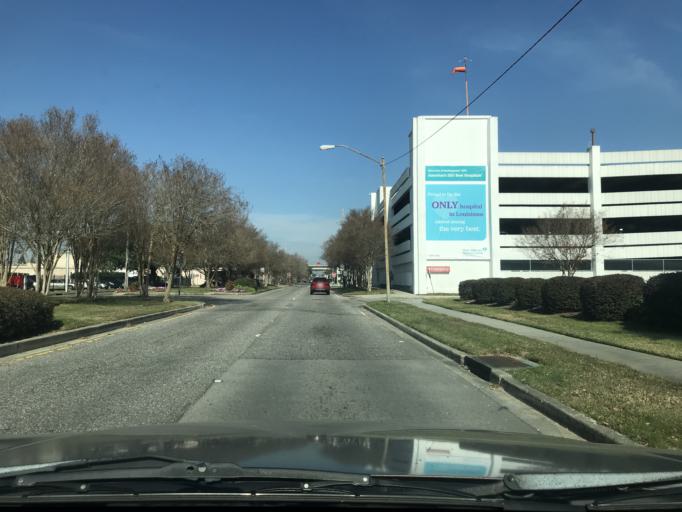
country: US
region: Louisiana
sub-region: Jefferson Parish
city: Marrero
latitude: 29.8920
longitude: -90.0960
